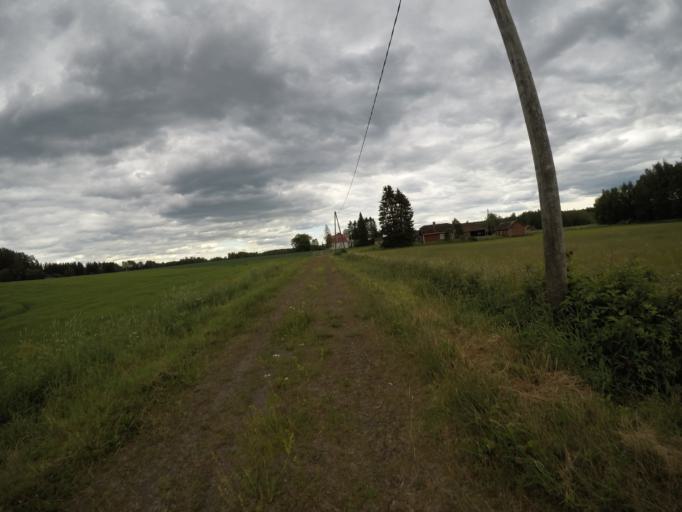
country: FI
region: Haeme
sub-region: Haemeenlinna
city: Haemeenlinna
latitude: 60.9723
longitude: 24.4585
